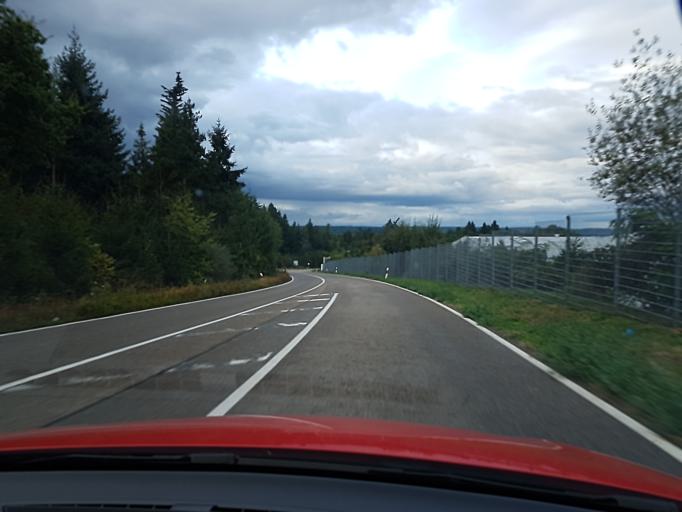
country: DE
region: Baden-Wuerttemberg
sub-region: Regierungsbezirk Stuttgart
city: Pfaffenhofen
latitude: 49.0475
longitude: 8.9864
